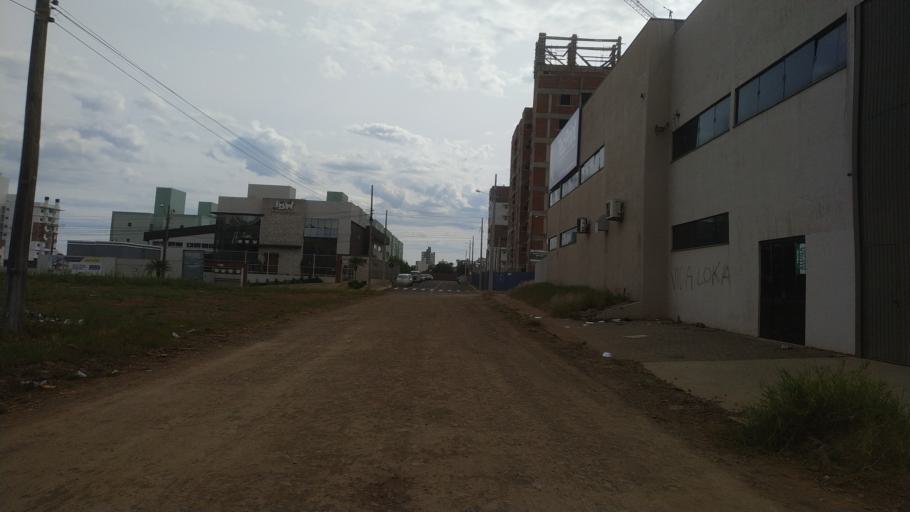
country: BR
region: Santa Catarina
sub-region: Chapeco
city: Chapeco
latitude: -27.1014
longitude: -52.5964
